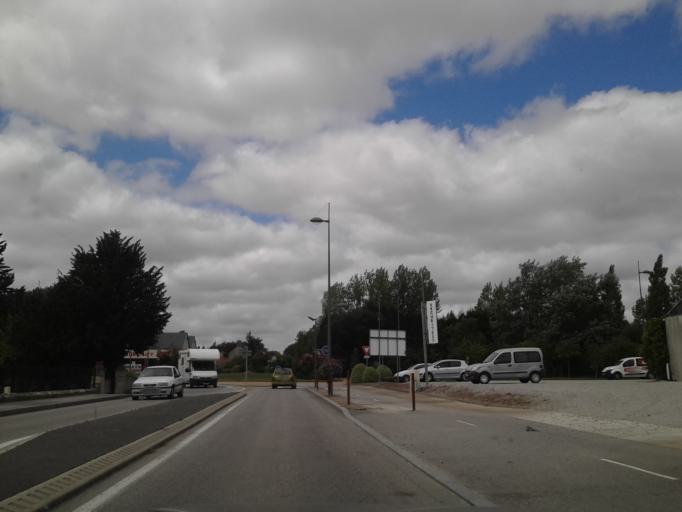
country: FR
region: Lower Normandy
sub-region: Departement de la Manche
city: Valognes
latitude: 49.5131
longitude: -1.4812
